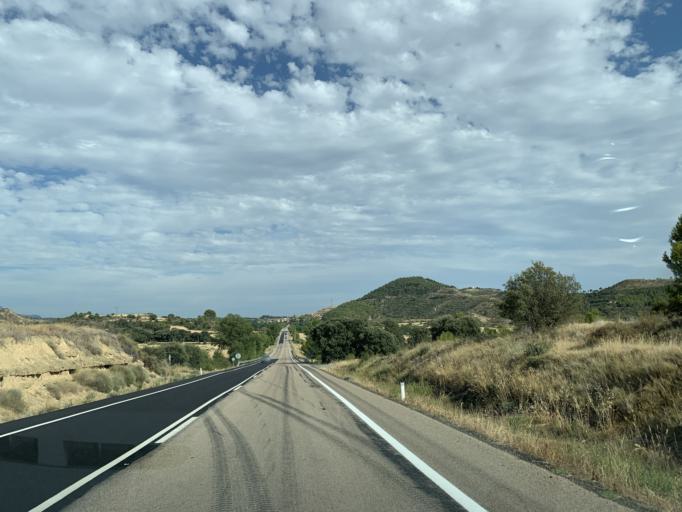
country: ES
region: Aragon
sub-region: Provincia de Huesca
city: Ayerbe
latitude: 42.2858
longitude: -0.7092
